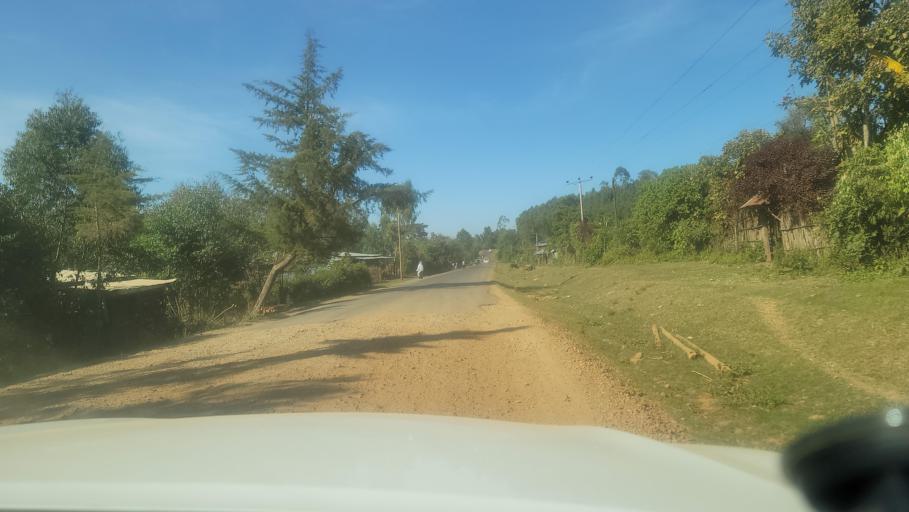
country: ET
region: Oromiya
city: Agaro
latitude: 7.7969
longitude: 36.4863
